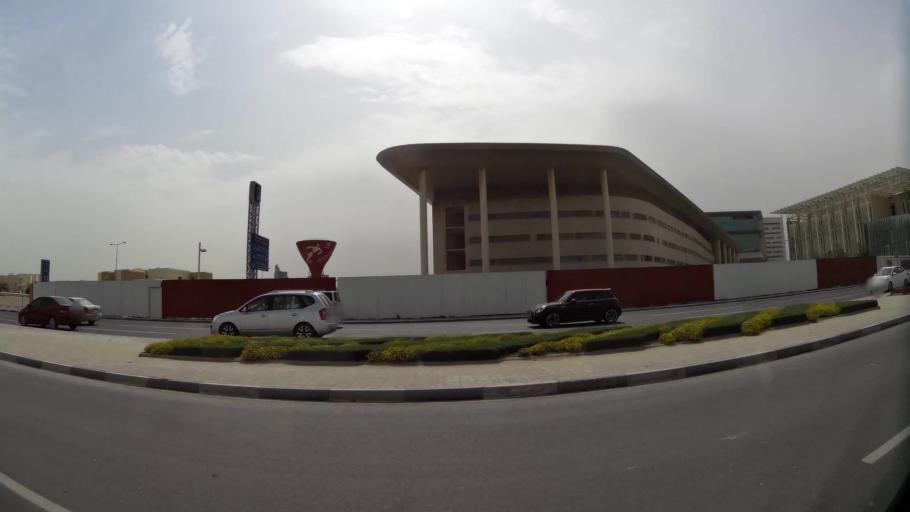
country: QA
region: Baladiyat ad Dawhah
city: Doha
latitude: 25.2954
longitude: 51.5111
